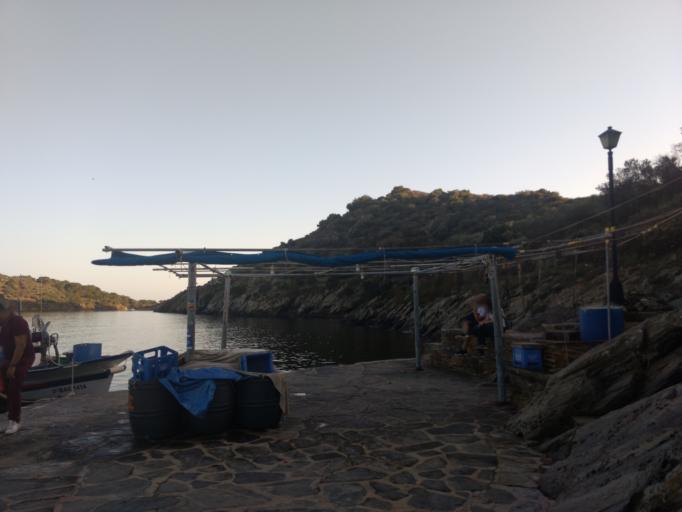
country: ES
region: Catalonia
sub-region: Provincia de Girona
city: Cadaques
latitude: 42.2929
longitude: 3.2866
